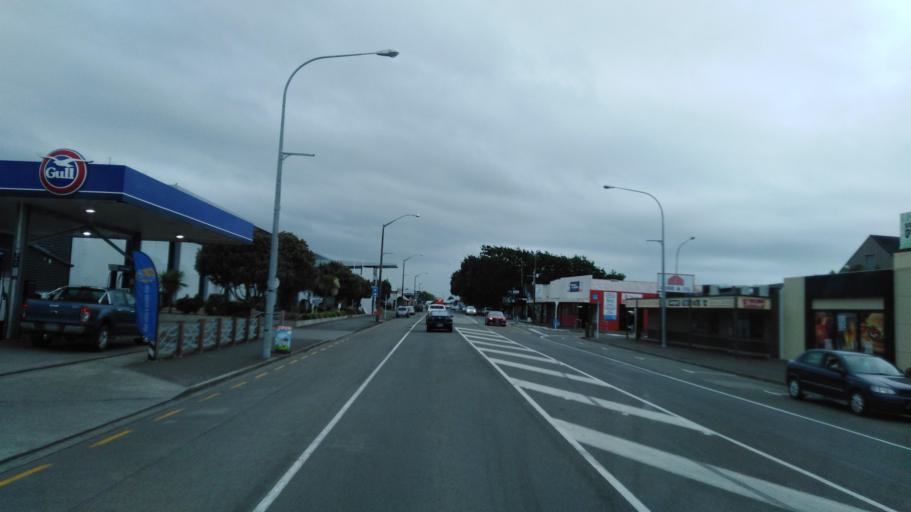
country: NZ
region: Manawatu-Wanganui
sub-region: Horowhenua District
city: Levin
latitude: -40.6242
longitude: 175.2843
